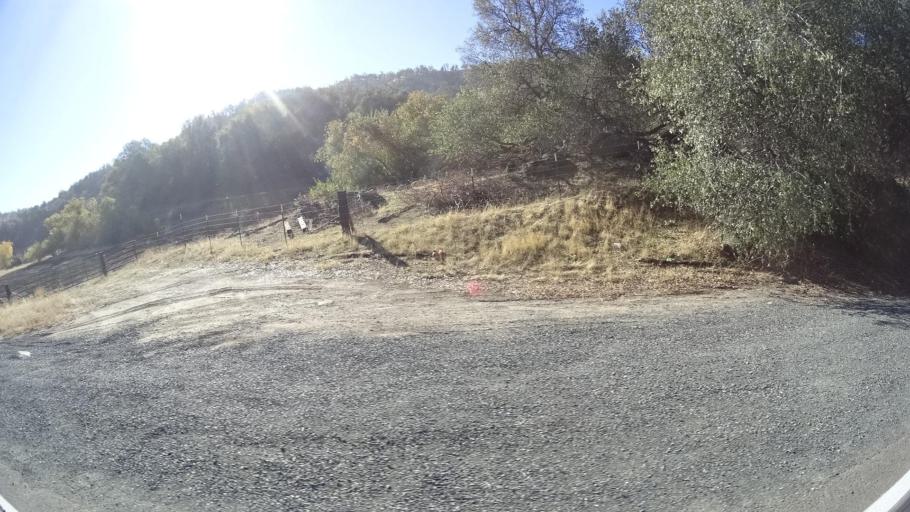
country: US
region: California
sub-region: Kern County
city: Alta Sierra
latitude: 35.7123
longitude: -118.7846
